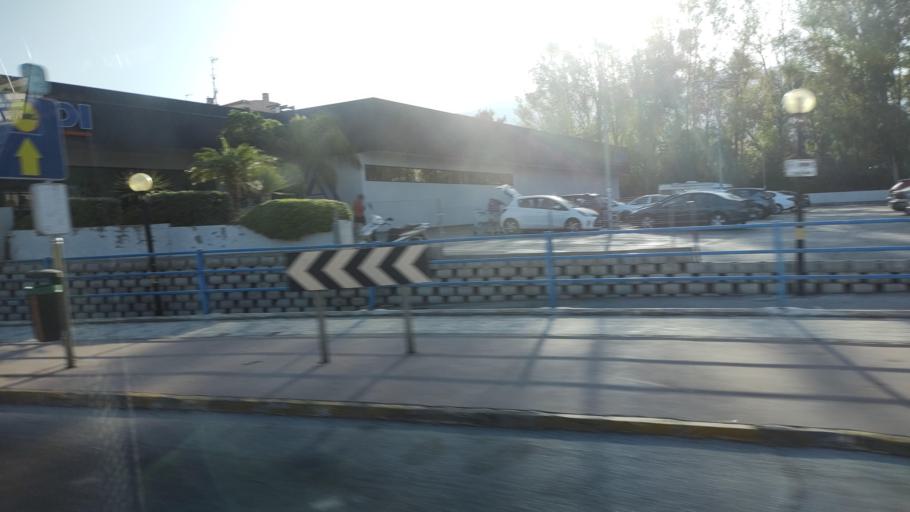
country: ES
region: Andalusia
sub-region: Provincia de Malaga
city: Torremolinos
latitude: 36.6324
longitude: -4.4996
